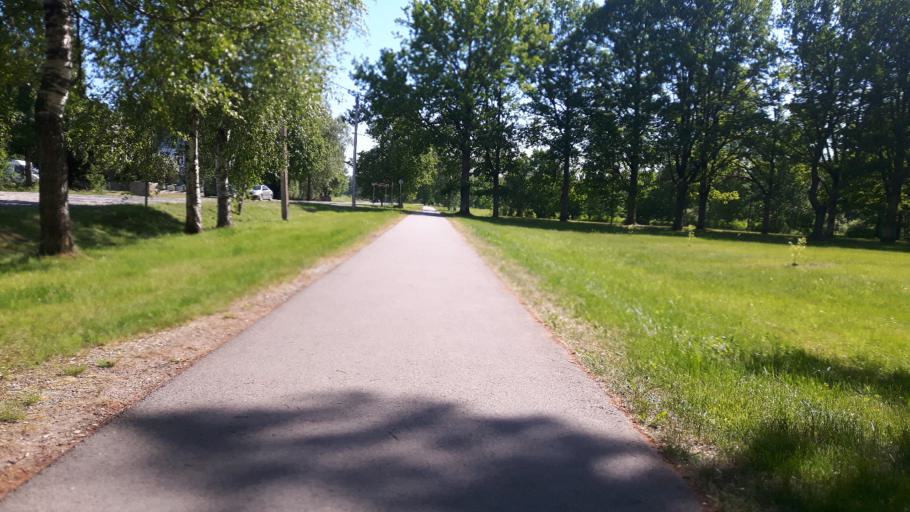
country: EE
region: Paernumaa
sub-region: Paikuse vald
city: Paikuse
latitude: 58.3971
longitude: 24.6412
